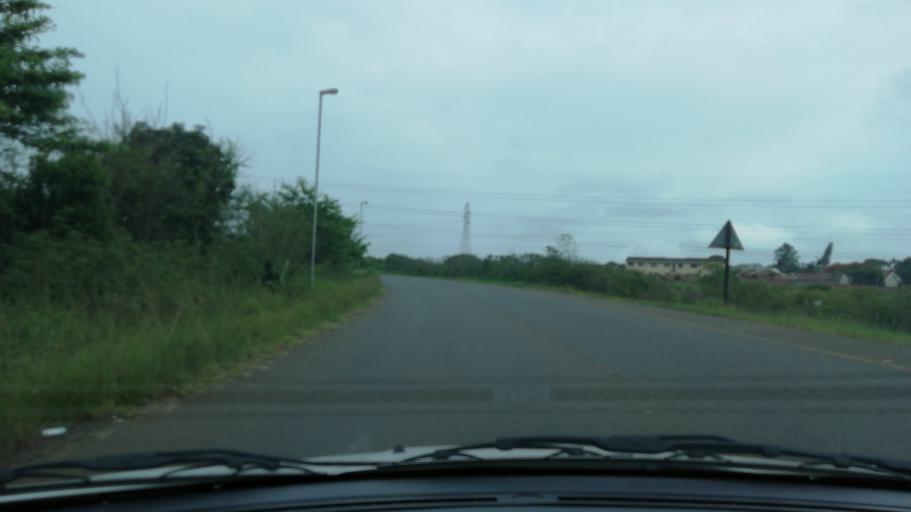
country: ZA
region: KwaZulu-Natal
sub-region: uThungulu District Municipality
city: Empangeni
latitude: -28.7351
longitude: 31.8887
